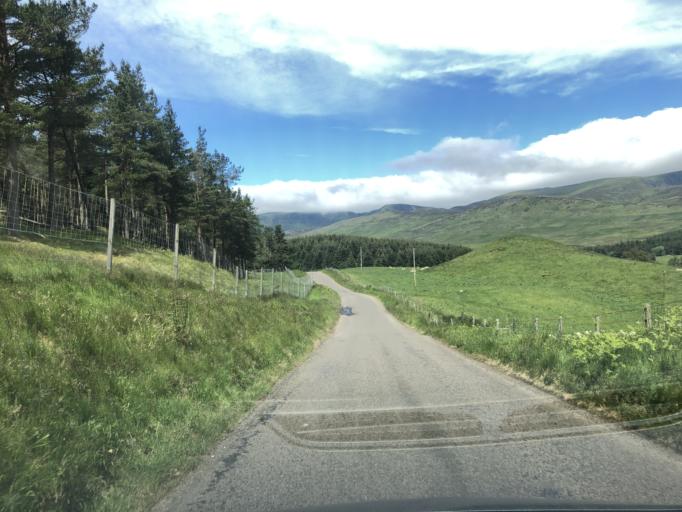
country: GB
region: Scotland
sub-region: Angus
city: Kirriemuir
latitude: 56.8214
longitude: -3.0605
